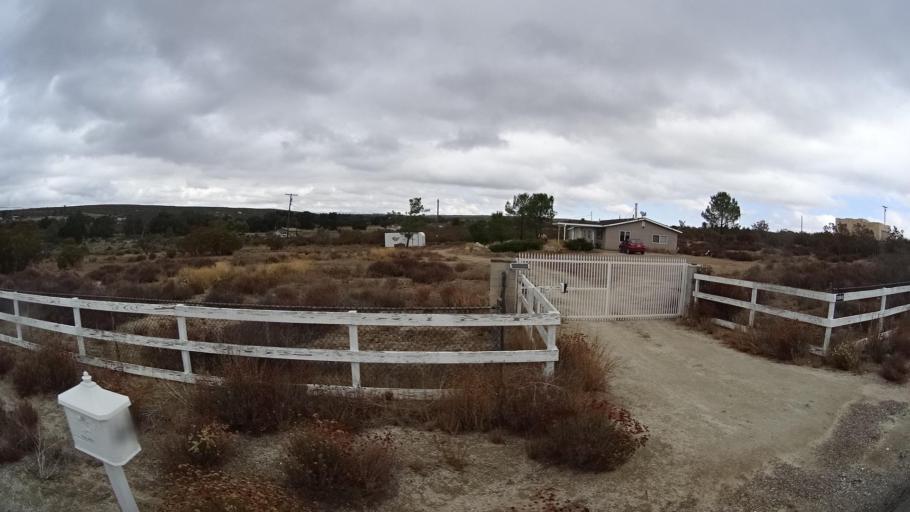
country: US
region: California
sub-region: San Diego County
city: Campo
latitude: 32.6050
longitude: -116.3434
